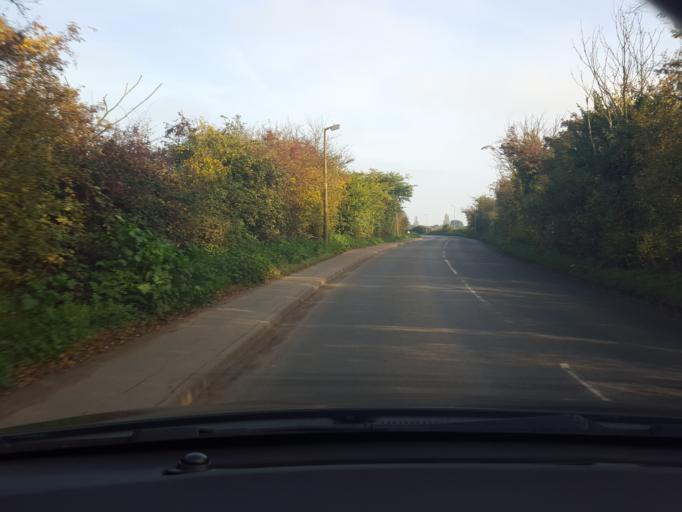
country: GB
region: England
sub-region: Essex
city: Frinton-on-Sea
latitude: 51.8506
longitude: 1.2406
